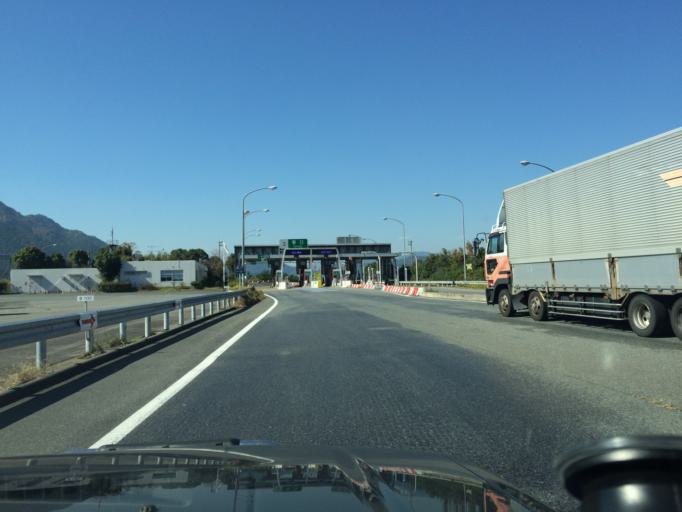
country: JP
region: Kyoto
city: Fukuchiyama
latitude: 35.1643
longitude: 135.1175
